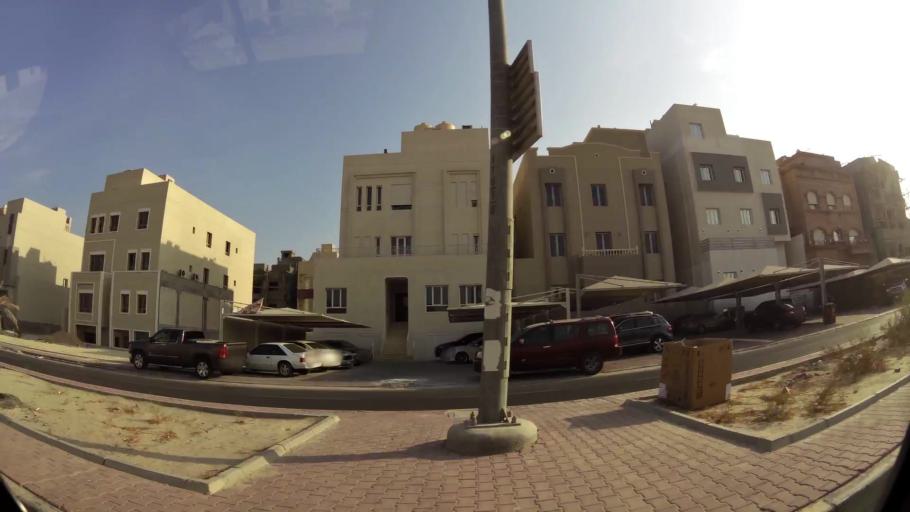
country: KW
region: Mubarak al Kabir
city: Mubarak al Kabir
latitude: 29.1978
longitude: 48.1059
